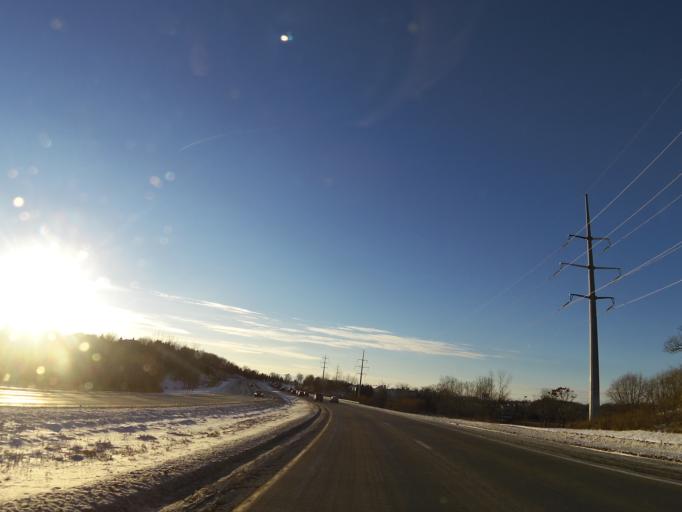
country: US
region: Minnesota
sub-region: Carver County
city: Chanhassen
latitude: 44.8629
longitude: -93.5004
